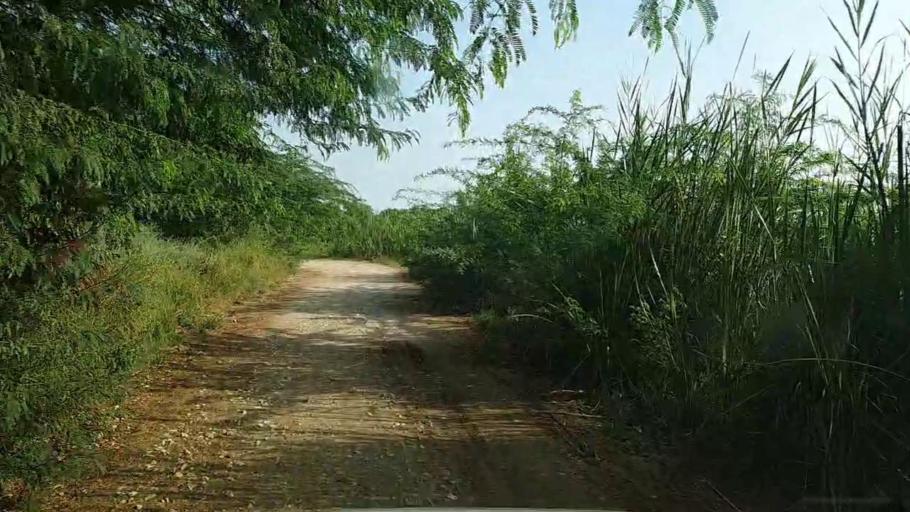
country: PK
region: Sindh
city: Pad Idan
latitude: 26.8334
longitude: 68.2414
